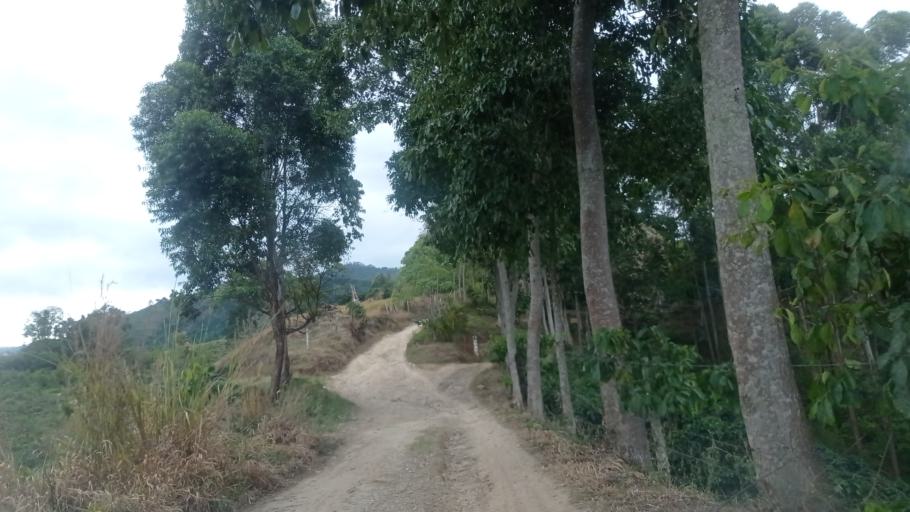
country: CO
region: Huila
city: Garzon
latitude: 2.0998
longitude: -75.6287
